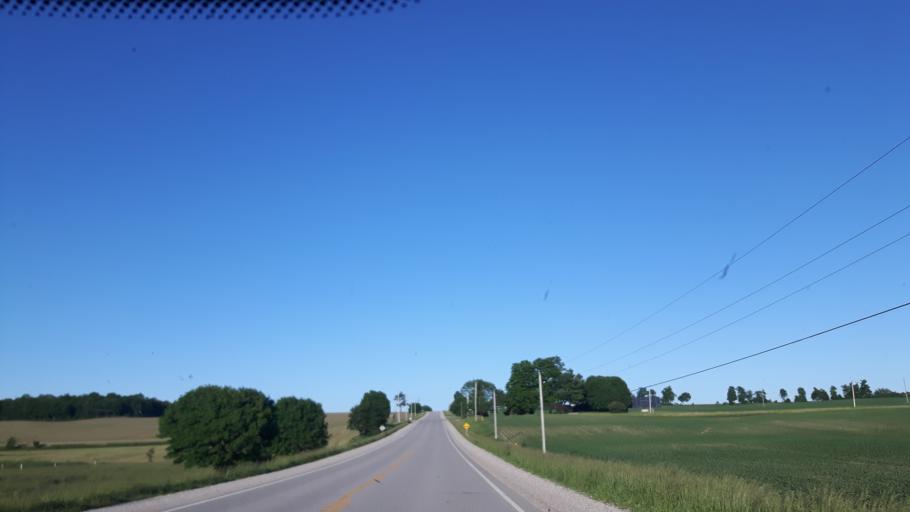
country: CA
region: Ontario
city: Goderich
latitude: 43.6427
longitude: -81.6265
